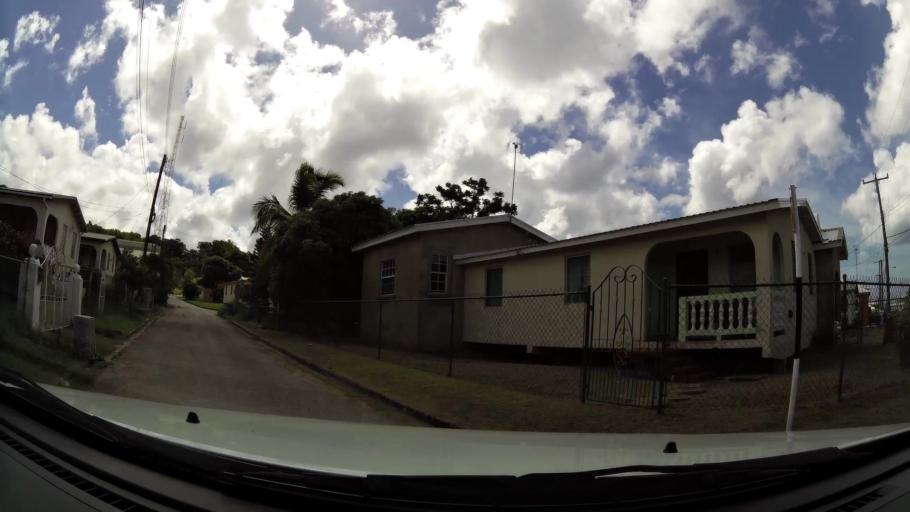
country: BB
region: Saint James
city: Holetown
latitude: 13.1510
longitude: -59.6246
